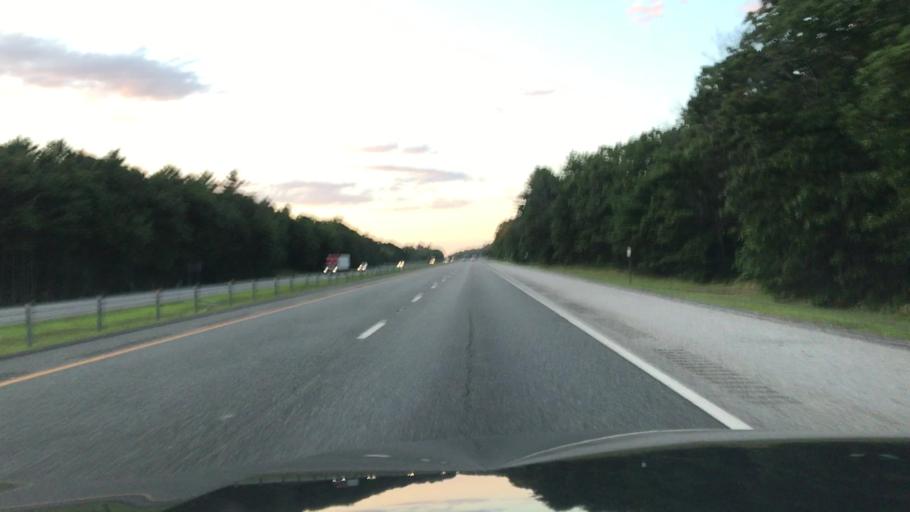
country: US
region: Rhode Island
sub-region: Kent County
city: West Greenwich
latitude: 41.5710
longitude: -71.6617
